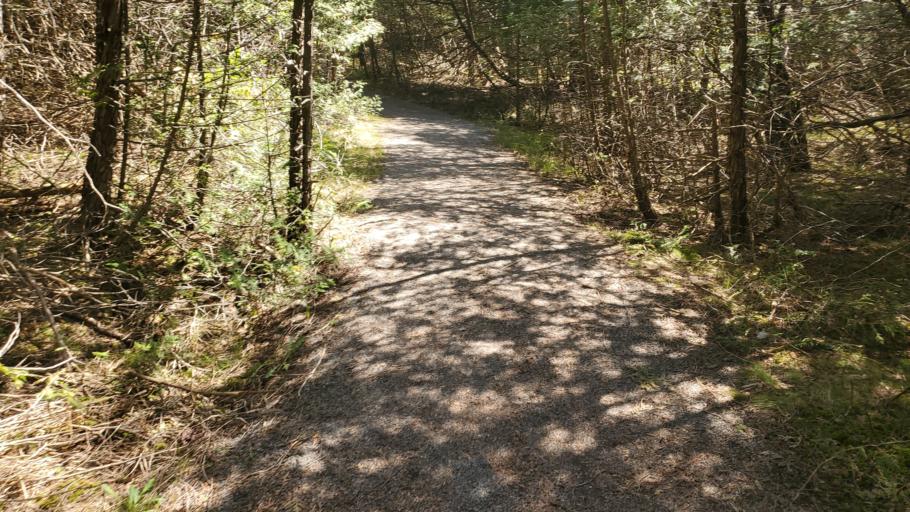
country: CA
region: Ontario
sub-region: Lanark County
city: Smiths Falls
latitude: 44.9133
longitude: -75.8279
